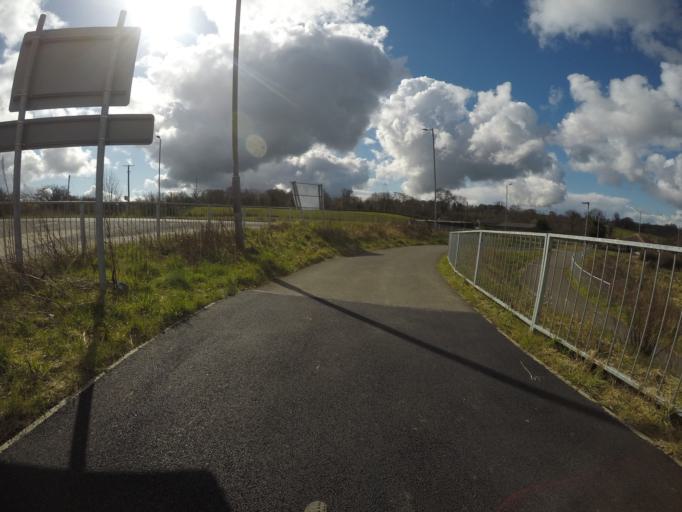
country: GB
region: Scotland
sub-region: North Ayrshire
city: Beith
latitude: 55.7385
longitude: -4.6597
